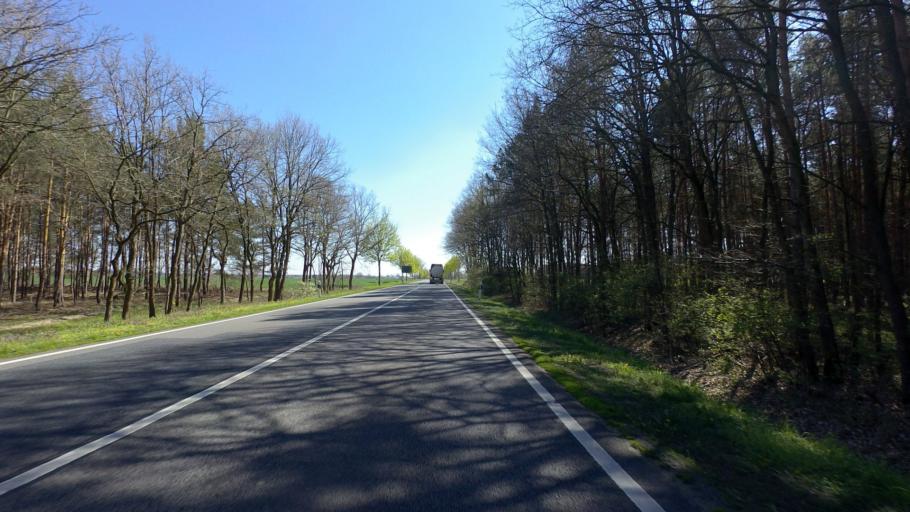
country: DE
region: Saxony-Anhalt
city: Pretzier
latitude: 52.7523
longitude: 11.2405
